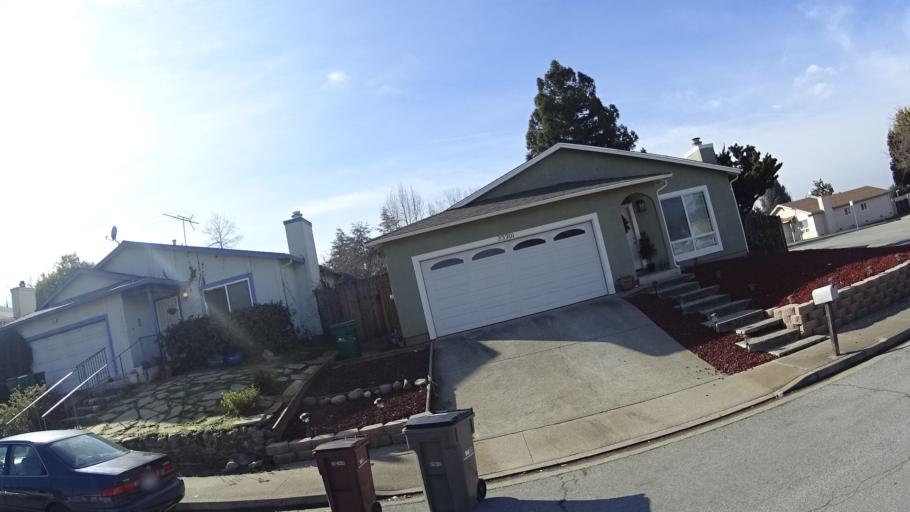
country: US
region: California
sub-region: Alameda County
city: Fairview
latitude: 37.6842
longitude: -122.0456
